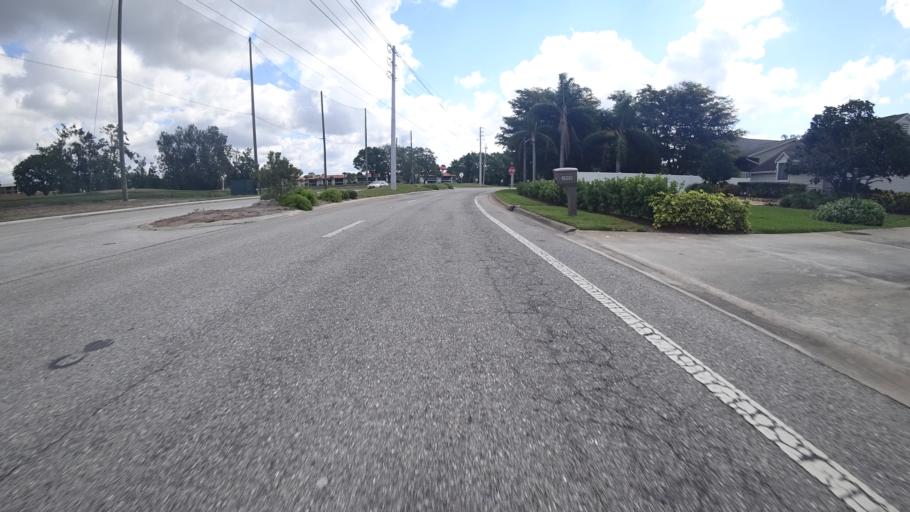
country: US
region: Florida
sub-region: Manatee County
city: Bayshore Gardens
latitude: 27.4291
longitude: -82.6030
